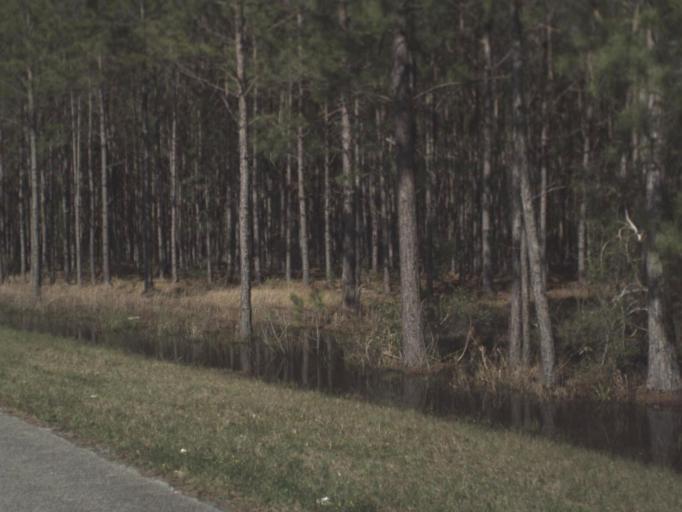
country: US
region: Florida
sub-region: Gulf County
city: Wewahitchka
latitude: 30.0064
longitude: -85.1742
